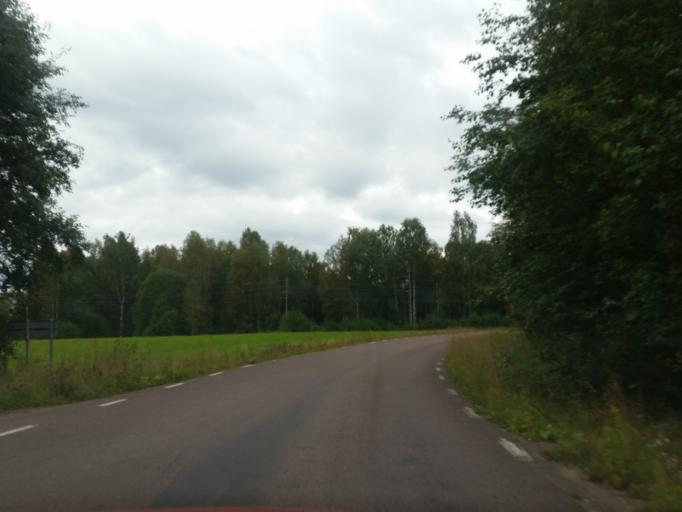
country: SE
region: Dalarna
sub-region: Gagnefs Kommun
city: Gagnef
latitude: 60.6681
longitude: 15.1567
